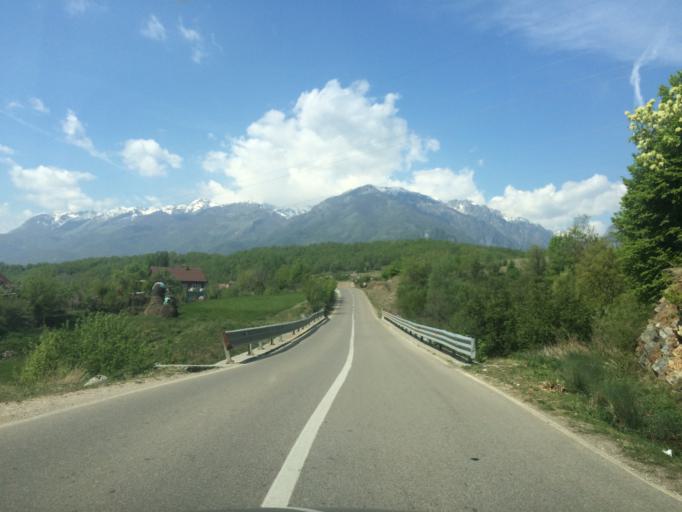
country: AL
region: Kukes
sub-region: Rrethi i Tropojes
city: Llugaj
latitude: 42.3770
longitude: 20.1289
